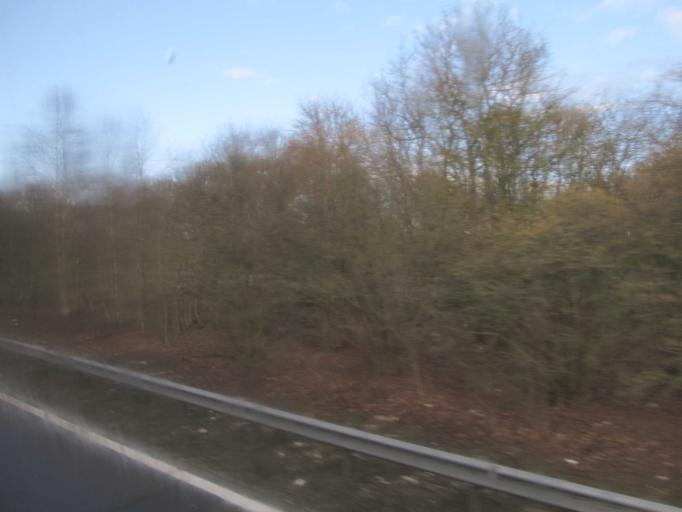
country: GB
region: England
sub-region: Hampshire
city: Overton
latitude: 51.2007
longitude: -1.2000
